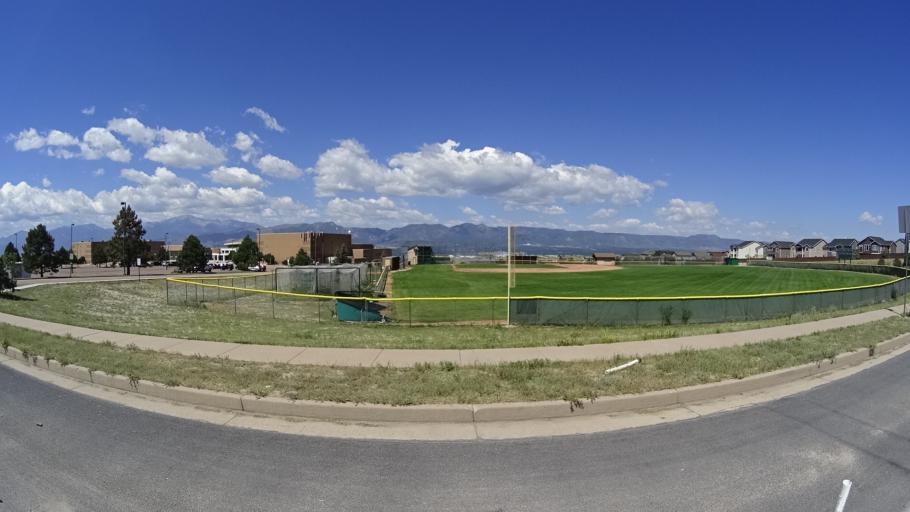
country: US
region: Colorado
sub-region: El Paso County
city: Black Forest
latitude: 38.9880
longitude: -104.7606
